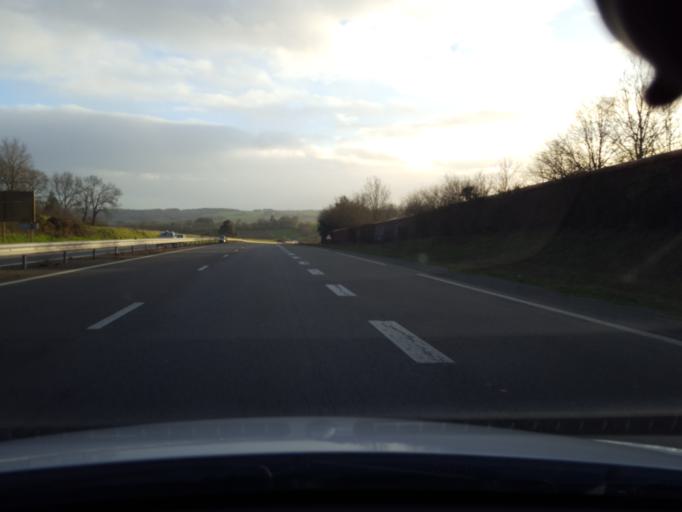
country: FR
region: Brittany
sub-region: Departement d'Ille-et-Vilaine
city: Guichen
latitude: 47.9591
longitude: -1.8160
